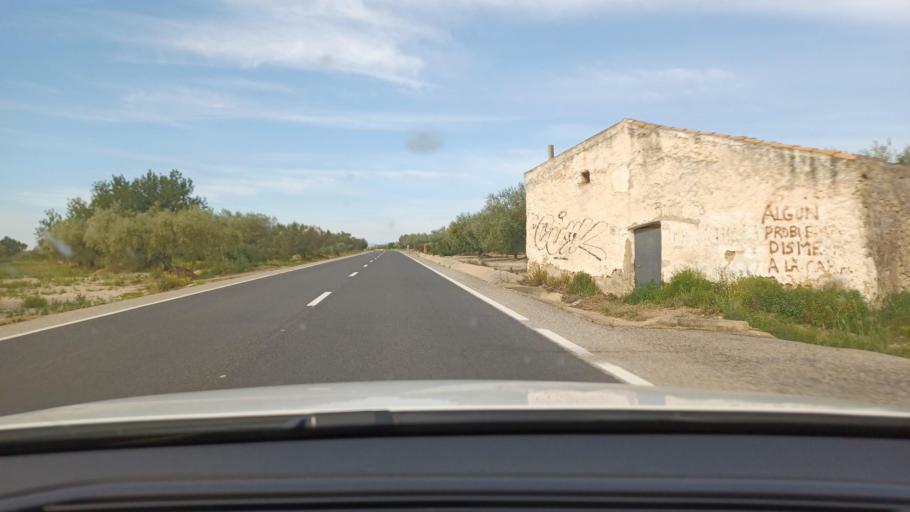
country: ES
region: Catalonia
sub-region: Provincia de Tarragona
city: Ulldecona
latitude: 40.6593
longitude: 0.4137
